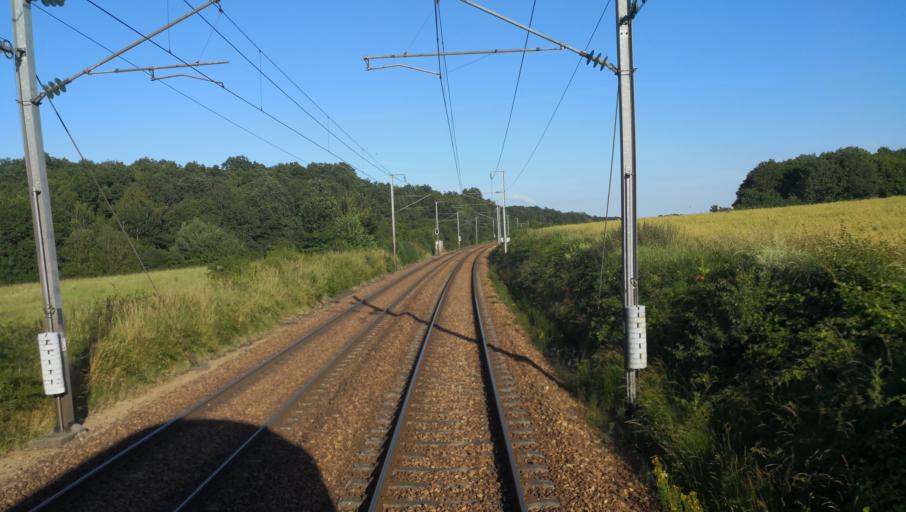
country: FR
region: Haute-Normandie
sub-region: Departement de l'Eure
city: Beaumont-le-Roger
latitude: 49.0204
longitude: 0.8290
